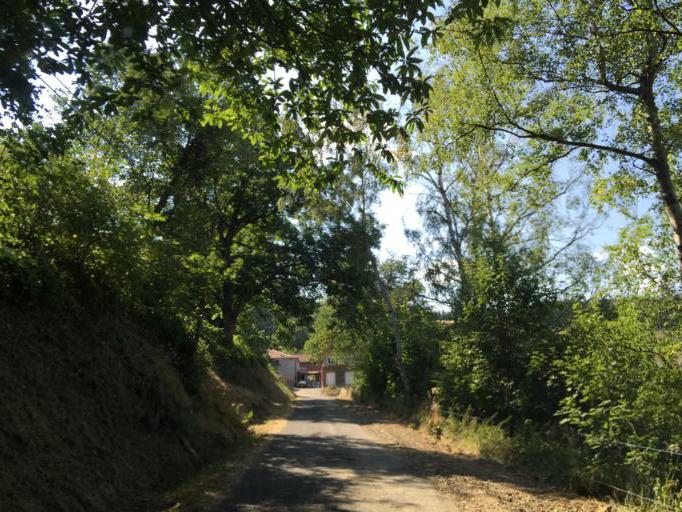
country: FR
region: Rhone-Alpes
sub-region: Departement de la Loire
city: Saint-Chamond
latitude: 45.4341
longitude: 4.4988
